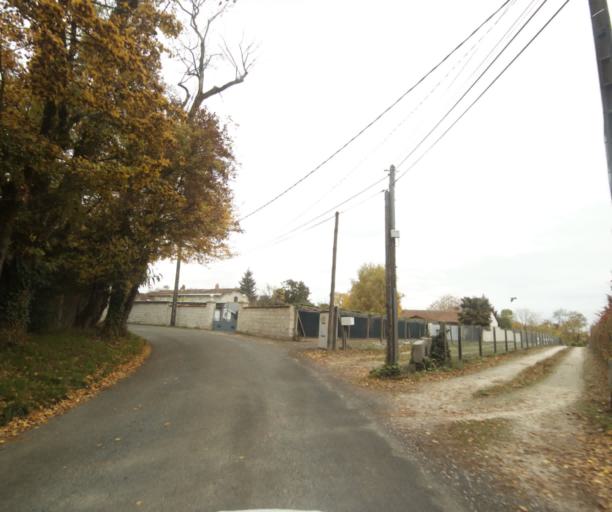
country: FR
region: Poitou-Charentes
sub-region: Departement de la Charente-Maritime
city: Saintes
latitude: 45.7381
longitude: -0.6730
